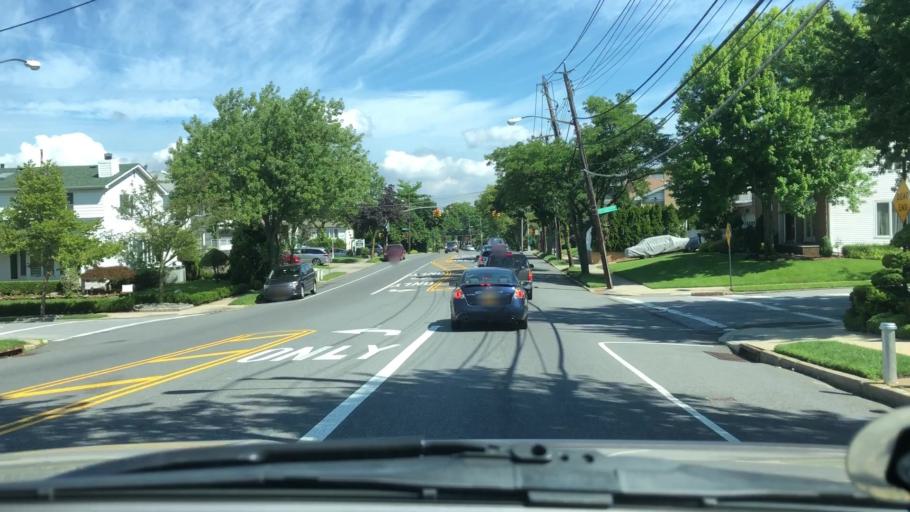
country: US
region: New York
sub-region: Richmond County
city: Staten Island
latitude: 40.6059
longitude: -74.1156
